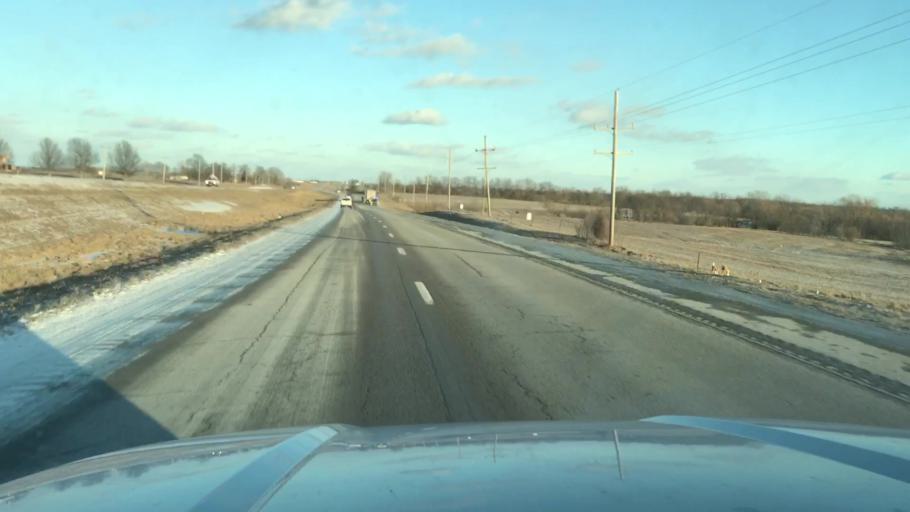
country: US
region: Missouri
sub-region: Clinton County
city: Cameron
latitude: 39.7544
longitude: -94.3353
